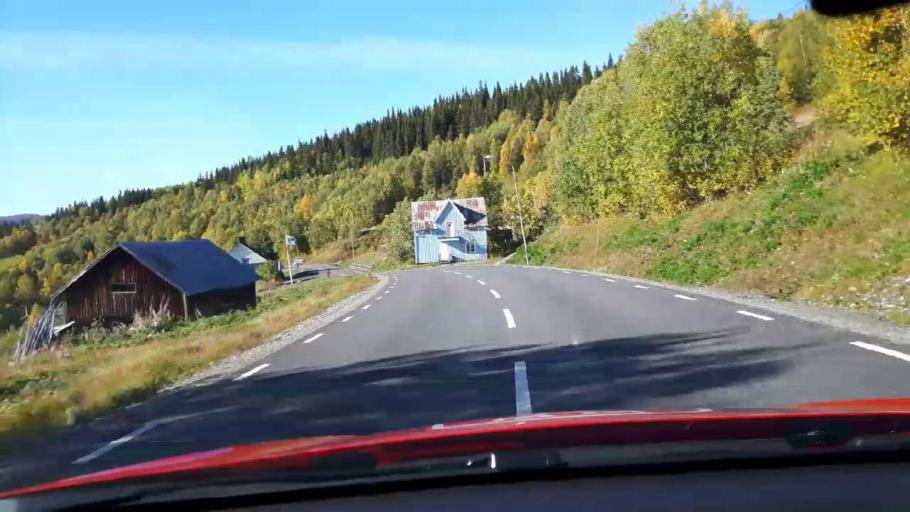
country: NO
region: Nord-Trondelag
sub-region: Royrvik
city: Royrvik
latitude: 64.8370
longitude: 14.1058
